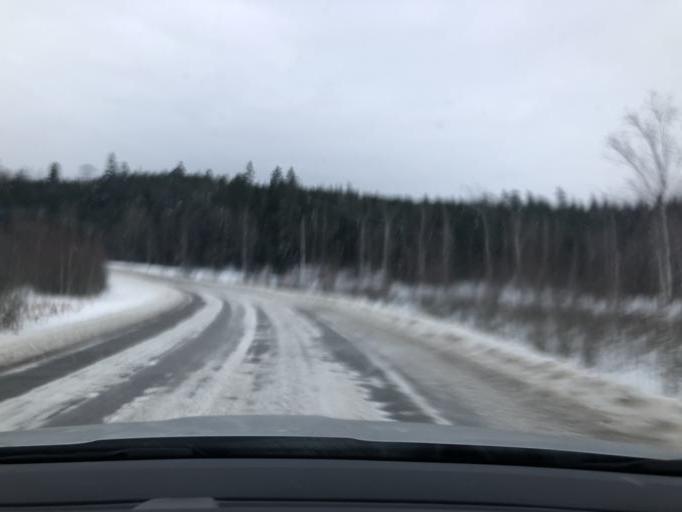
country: SE
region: OEstergoetland
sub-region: Kinda Kommun
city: Kisa
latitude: 58.0242
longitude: 15.7647
